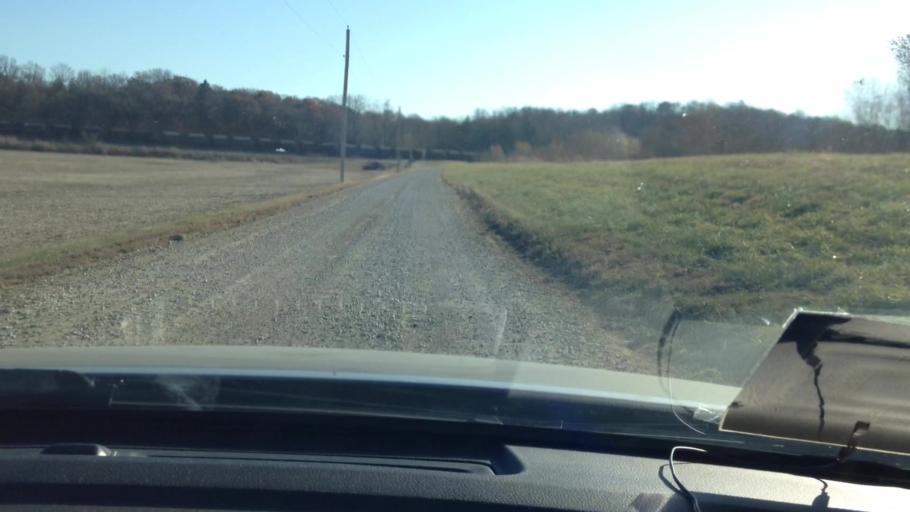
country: US
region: Kansas
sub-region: Leavenworth County
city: Leavenworth
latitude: 39.3289
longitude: -94.8614
